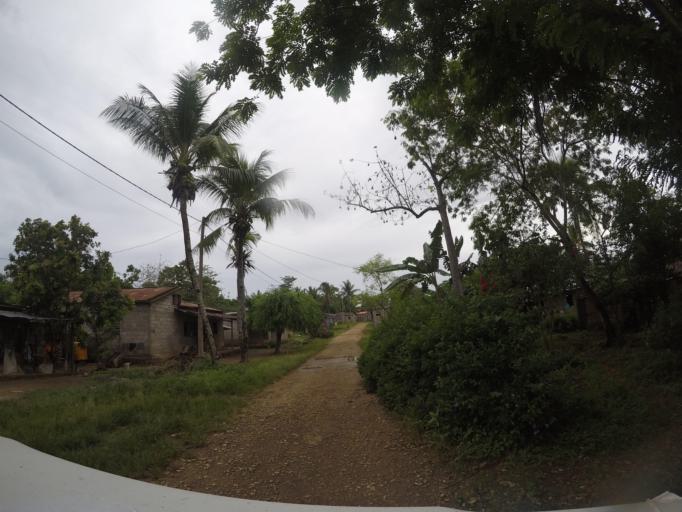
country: TL
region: Lautem
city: Lospalos
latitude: -8.5320
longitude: 127.0013
